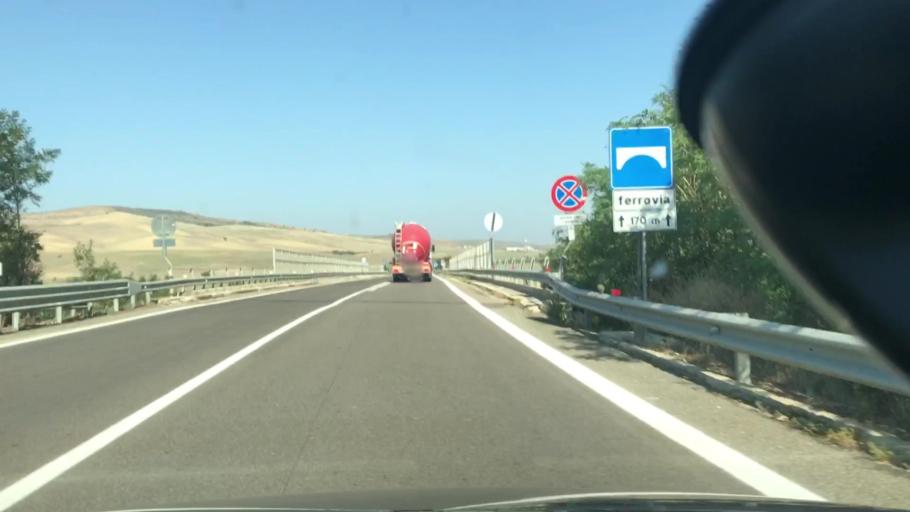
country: IT
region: Basilicate
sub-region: Provincia di Matera
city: Irsina
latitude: 40.7893
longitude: 16.2866
